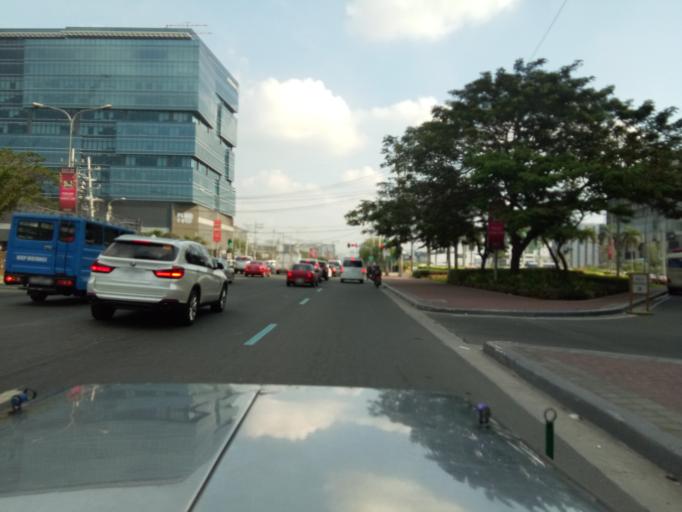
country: PH
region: Metro Manila
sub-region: Makati City
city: Makati City
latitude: 14.5242
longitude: 120.9906
